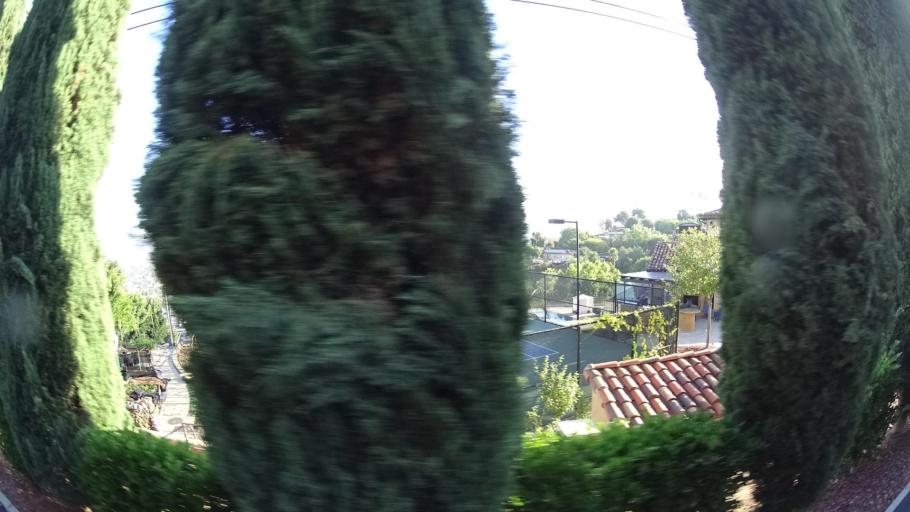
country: US
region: California
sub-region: San Diego County
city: Casa de Oro-Mount Helix
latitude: 32.7723
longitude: -116.9639
